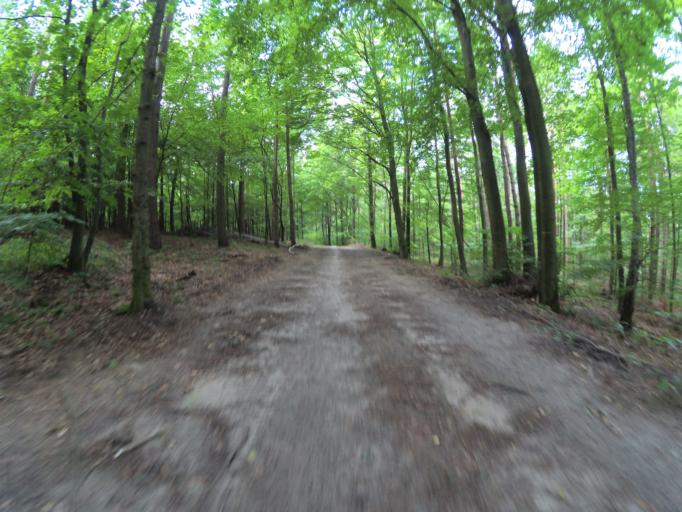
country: PL
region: Pomeranian Voivodeship
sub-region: Gdynia
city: Wielki Kack
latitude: 54.5049
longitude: 18.4481
